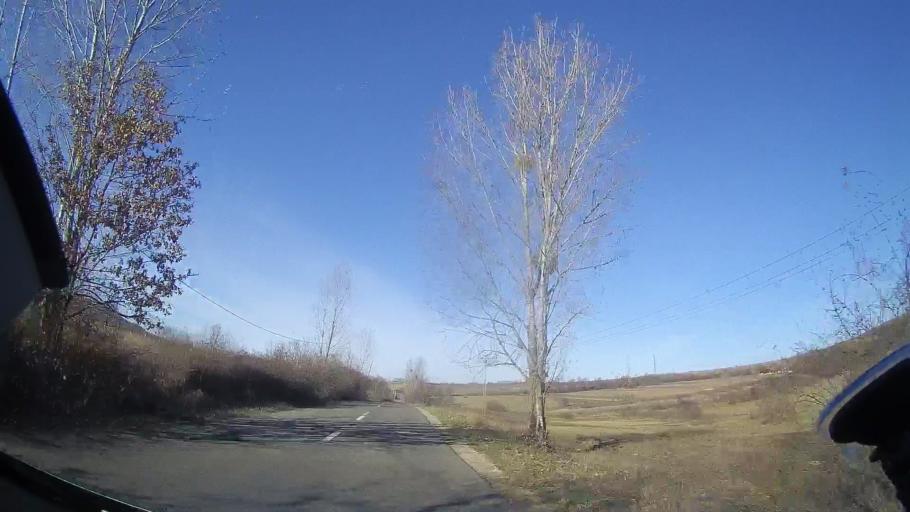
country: RO
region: Bihor
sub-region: Comuna Suncuius
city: Balnaca
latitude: 46.9664
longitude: 22.5510
